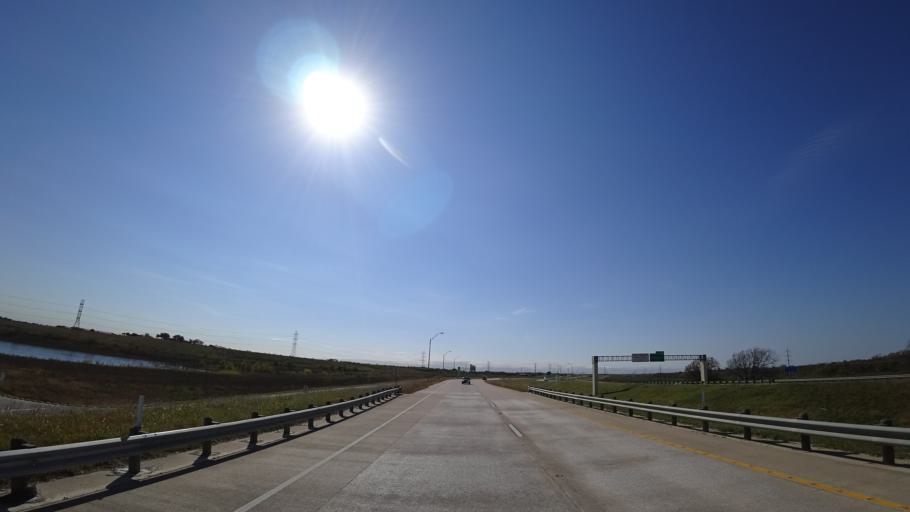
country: US
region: Texas
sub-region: Travis County
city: Garfield
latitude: 30.1852
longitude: -97.6283
